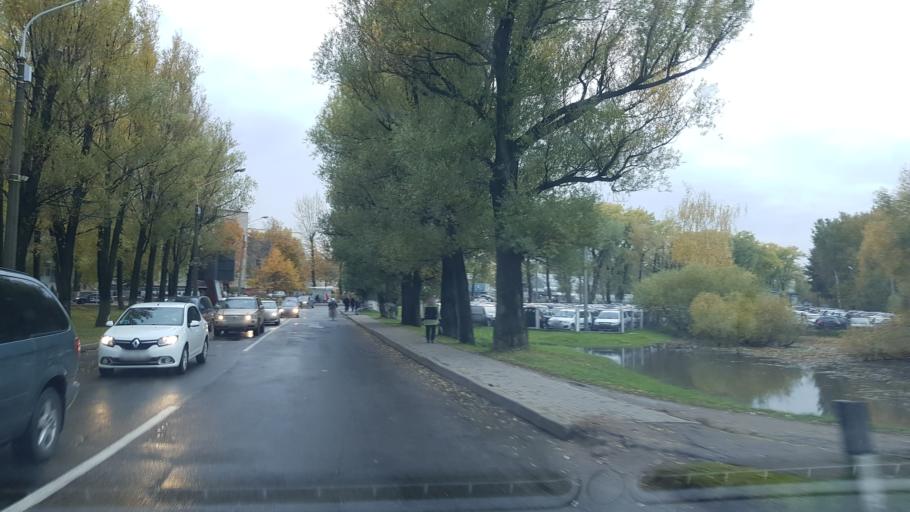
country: BY
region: Minsk
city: Syenitsa
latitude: 53.8443
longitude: 27.5457
